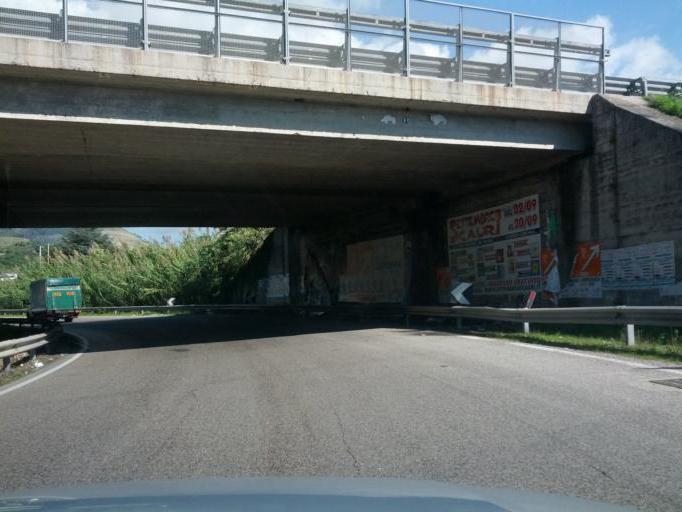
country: IT
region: Latium
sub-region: Provincia di Latina
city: Penitro
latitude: 41.2669
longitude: 13.6842
